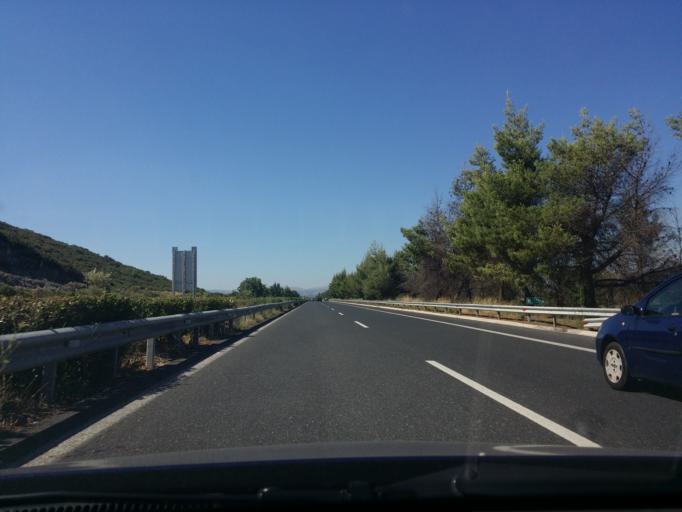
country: GR
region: Peloponnese
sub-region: Nomos Arkadias
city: Tripoli
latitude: 37.5699
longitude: 22.4273
